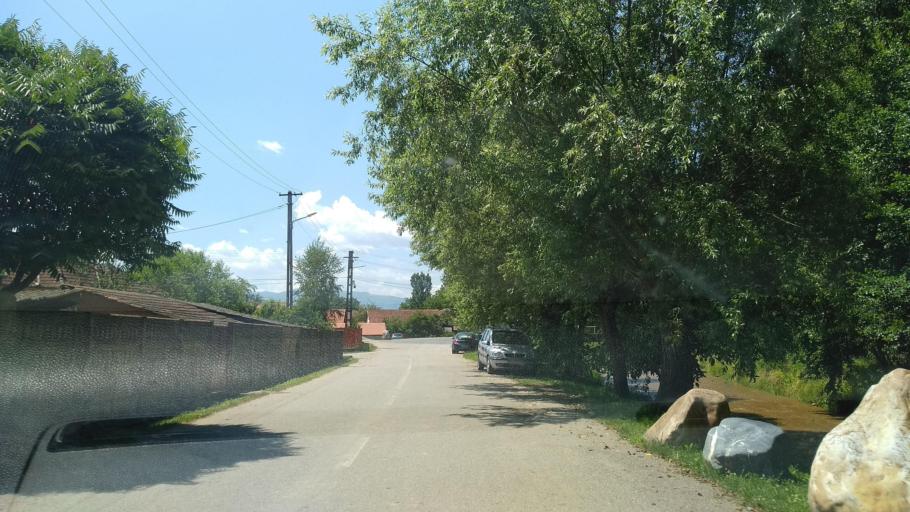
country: RO
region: Hunedoara
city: Densus
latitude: 45.5761
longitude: 22.8376
